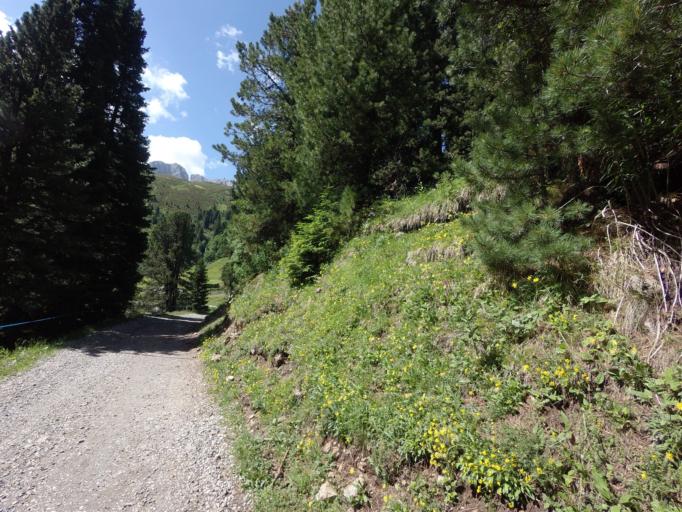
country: IT
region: Trentino-Alto Adige
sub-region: Provincia di Trento
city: Mazzin
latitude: 46.5057
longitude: 11.6547
